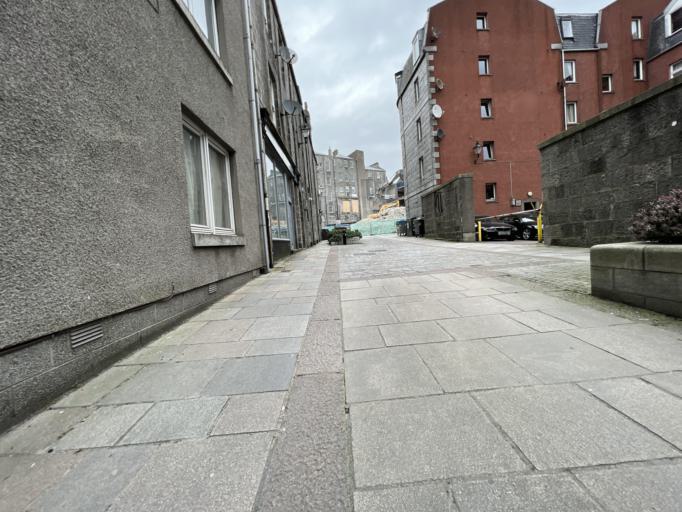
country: GB
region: Scotland
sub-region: Aberdeen City
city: Aberdeen
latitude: 57.1456
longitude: -2.0984
